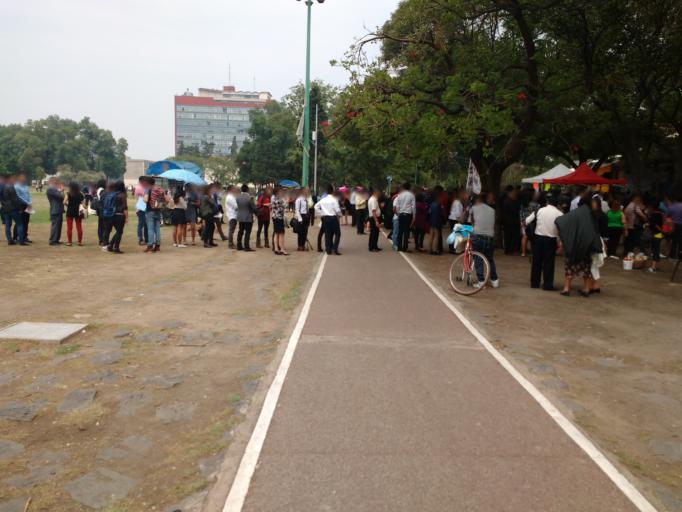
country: MX
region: Mexico City
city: Magdalena Contreras
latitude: 19.3324
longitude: -99.1859
